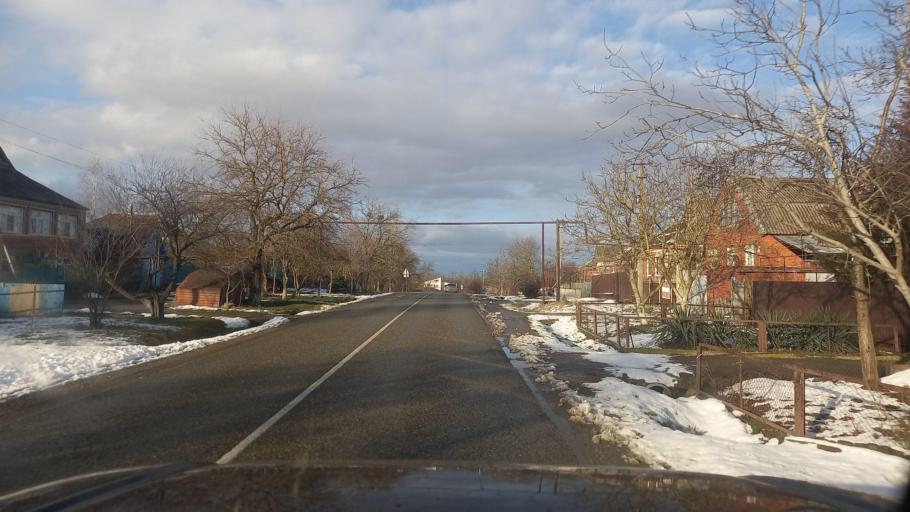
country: RU
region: Krasnodarskiy
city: Smolenskaya
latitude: 44.7738
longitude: 38.8458
